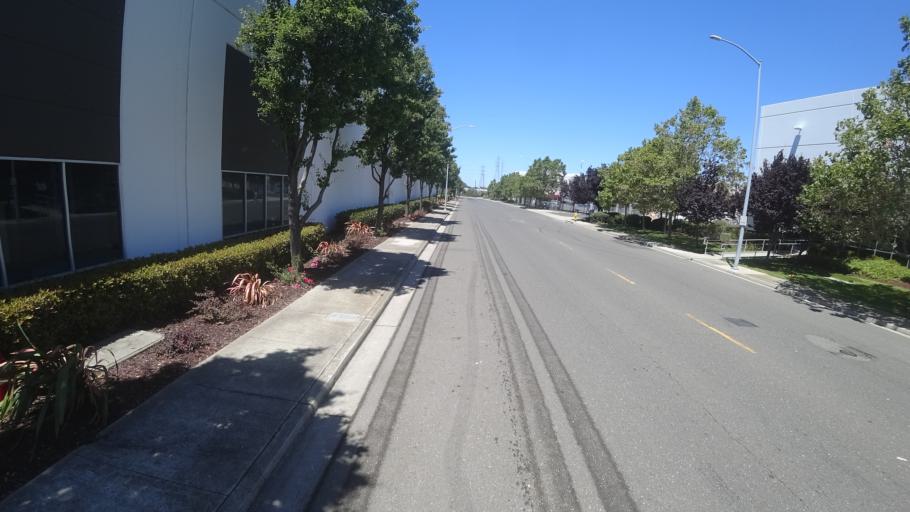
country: US
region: California
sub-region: Alameda County
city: Hayward
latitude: 37.6223
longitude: -122.1149
